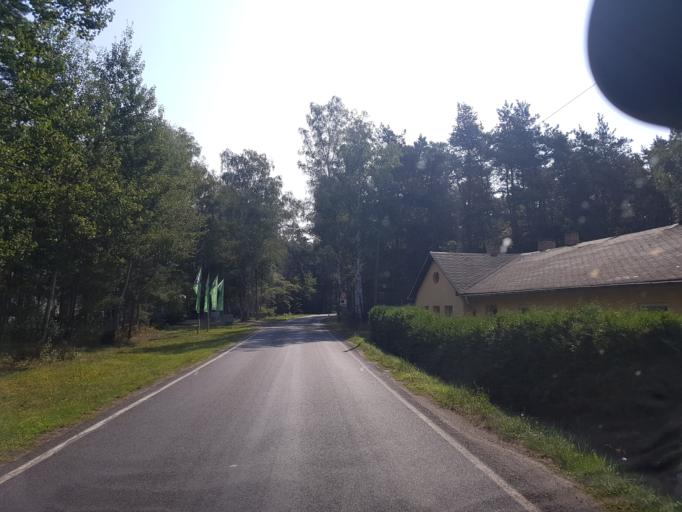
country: DE
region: Brandenburg
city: Lauchhammer
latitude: 51.5107
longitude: 13.7306
